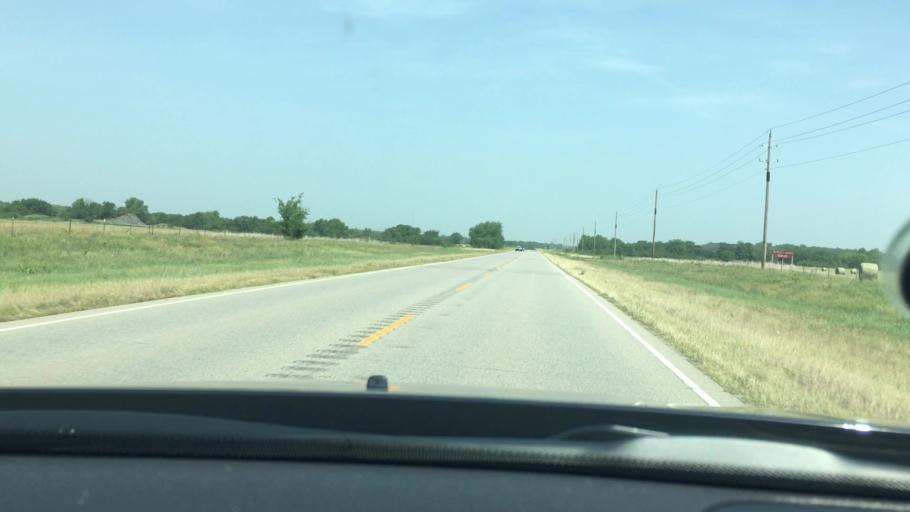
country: US
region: Oklahoma
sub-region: Atoka County
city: Atoka
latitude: 34.4274
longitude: -96.1949
